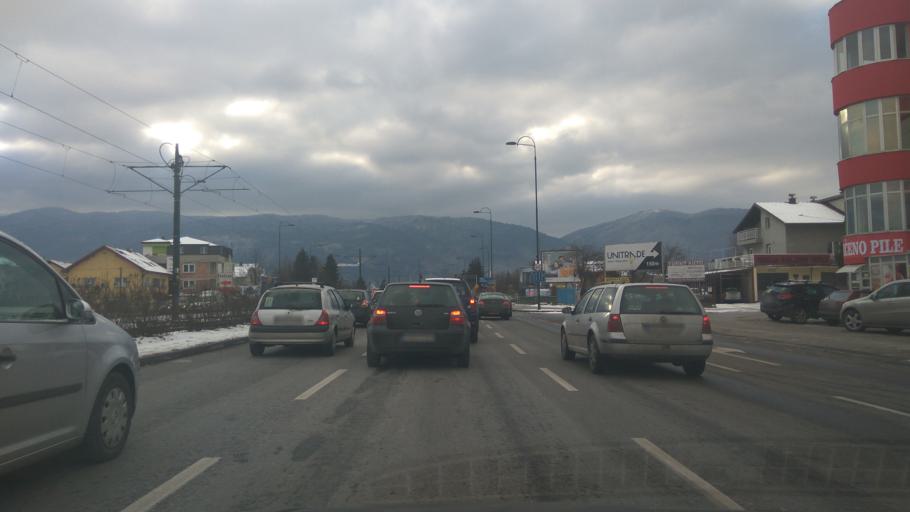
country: BA
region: Federation of Bosnia and Herzegovina
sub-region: Kanton Sarajevo
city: Sarajevo
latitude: 43.8387
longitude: 18.3191
